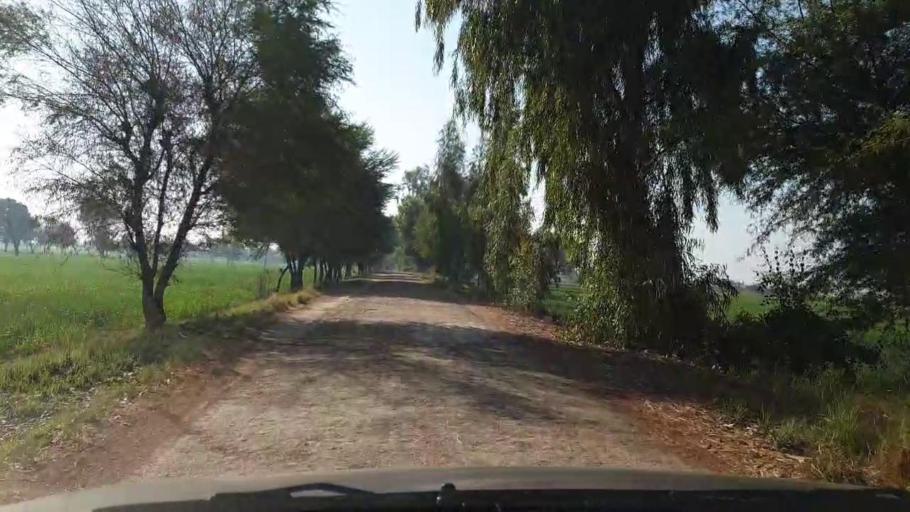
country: PK
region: Sindh
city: Jhol
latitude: 25.9462
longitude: 68.8474
